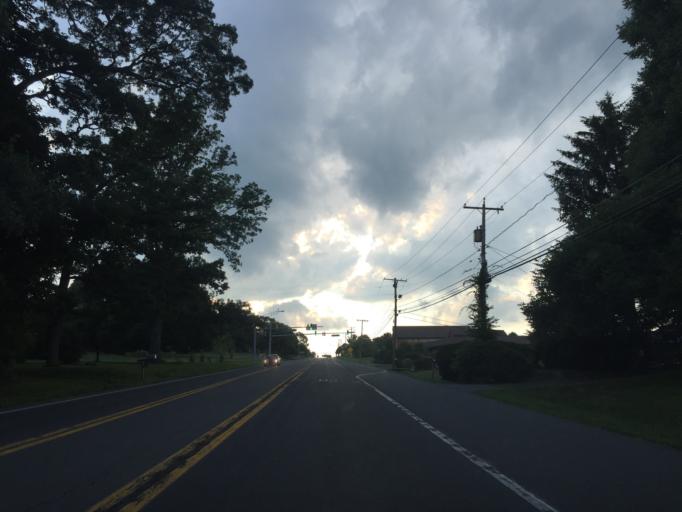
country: US
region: Maryland
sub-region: Harford County
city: Fallston
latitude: 39.5265
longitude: -76.4322
